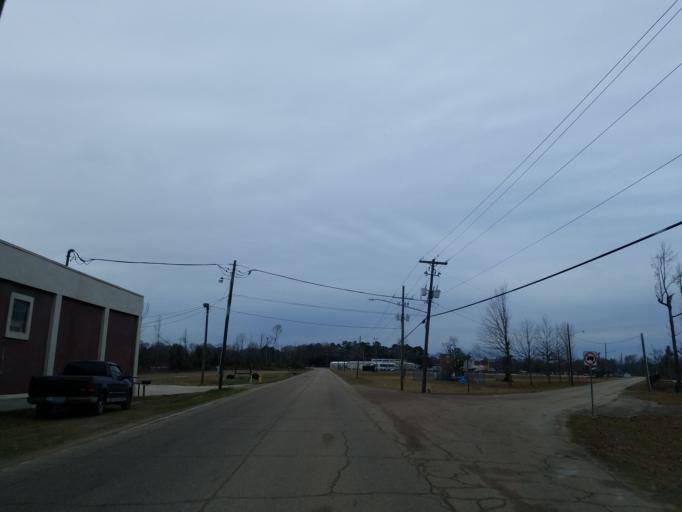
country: US
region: Mississippi
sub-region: Forrest County
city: Hattiesburg
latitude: 31.3114
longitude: -89.2810
